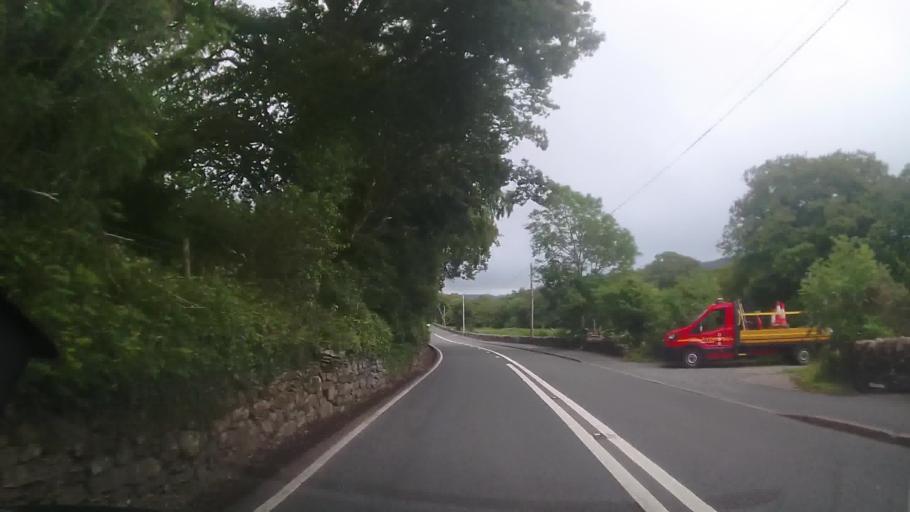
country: GB
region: Wales
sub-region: Conwy
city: Betws-y-Coed
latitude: 53.0958
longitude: -3.8851
